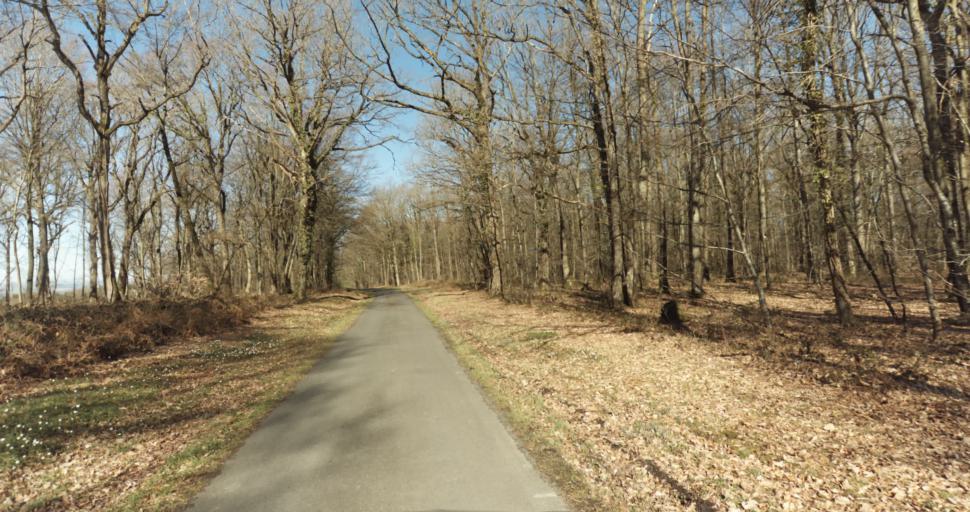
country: FR
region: Lower Normandy
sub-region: Departement de l'Orne
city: Trun
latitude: 48.9290
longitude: 0.0662
